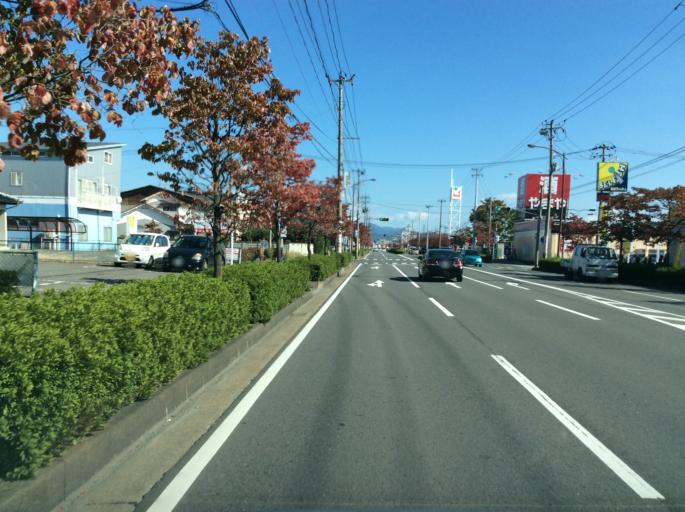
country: JP
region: Fukushima
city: Koriyama
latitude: 37.3694
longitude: 140.3545
